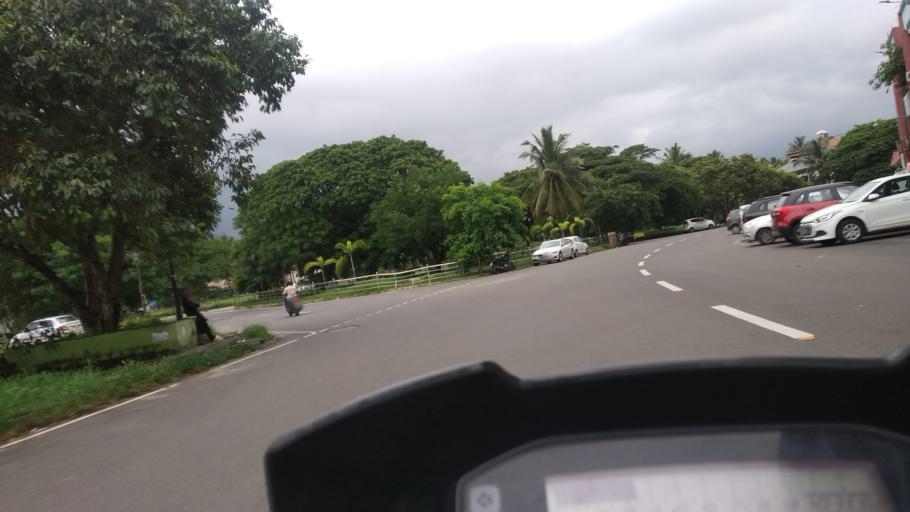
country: IN
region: Kerala
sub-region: Ernakulam
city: Elur
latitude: 9.9982
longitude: 76.3000
